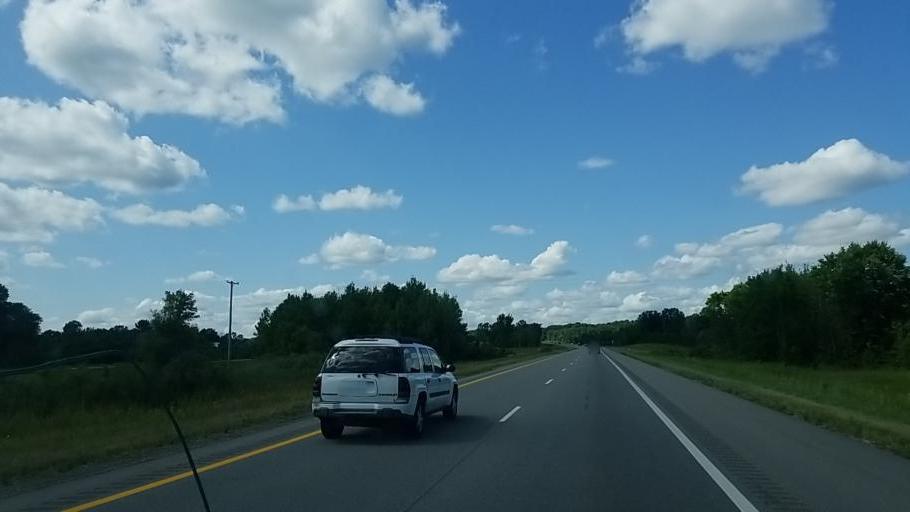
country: US
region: Michigan
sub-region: Mecosta County
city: Big Rapids
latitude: 43.6192
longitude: -85.4975
